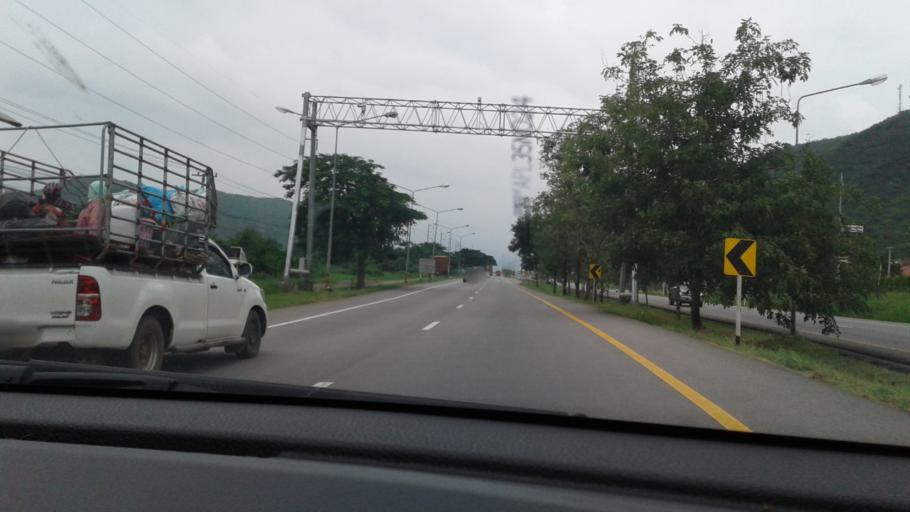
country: TH
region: Prachuap Khiri Khan
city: Prachuap Khiri Khan
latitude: 11.8988
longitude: 99.7944
